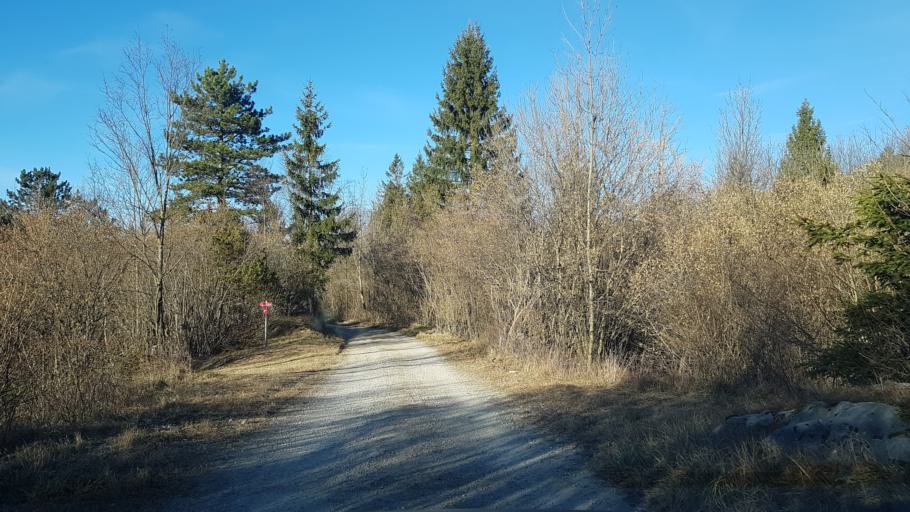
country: SI
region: Nova Gorica
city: Kromberk
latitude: 46.0193
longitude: 13.6995
